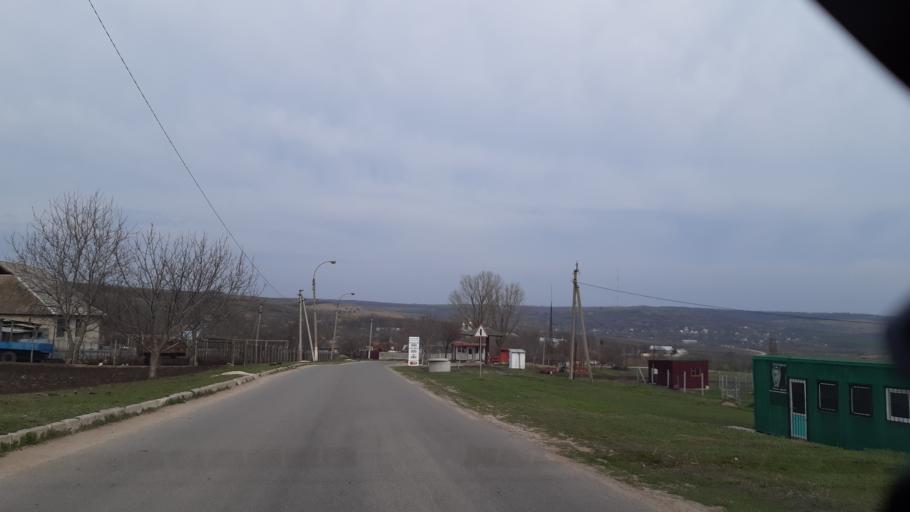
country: MD
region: Soldanesti
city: Soldanesti
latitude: 47.6841
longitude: 28.7724
